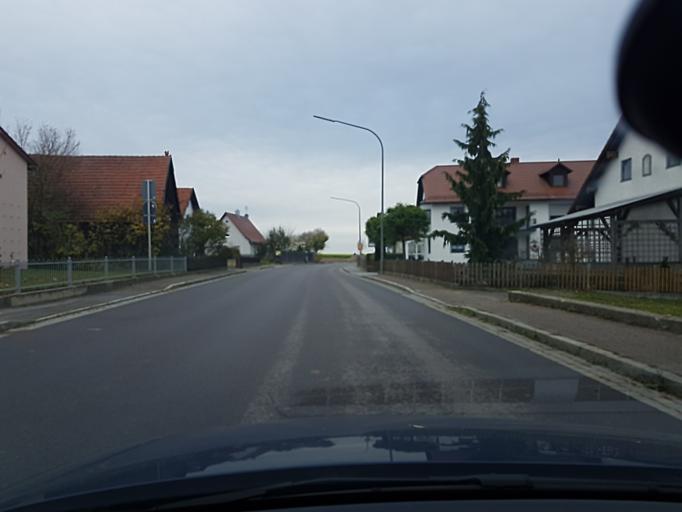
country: DE
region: Bavaria
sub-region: Upper Palatinate
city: Schierling
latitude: 48.8150
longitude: 12.1714
